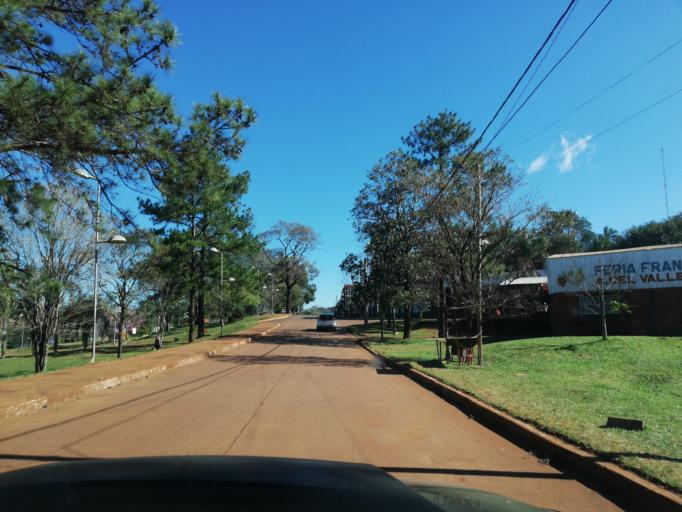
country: AR
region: Misiones
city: Aristobulo del Valle
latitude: -27.0944
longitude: -54.8910
